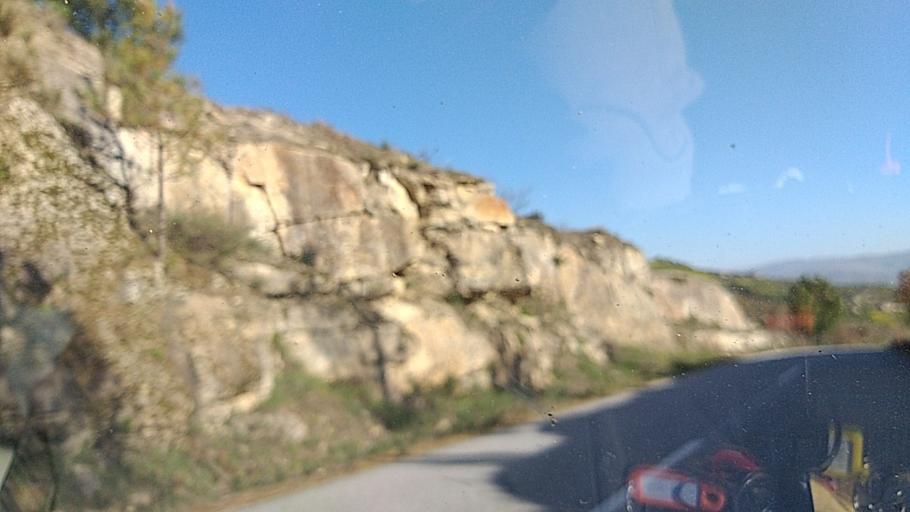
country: PT
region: Guarda
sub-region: Fornos de Algodres
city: Fornos de Algodres
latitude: 40.6376
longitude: -7.4799
